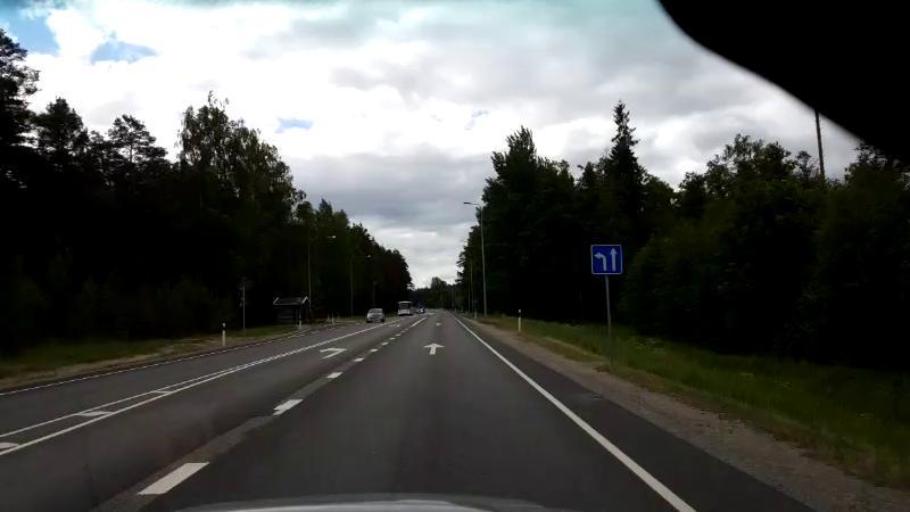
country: EE
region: Paernumaa
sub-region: Paikuse vald
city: Paikuse
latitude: 58.3234
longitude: 24.5978
